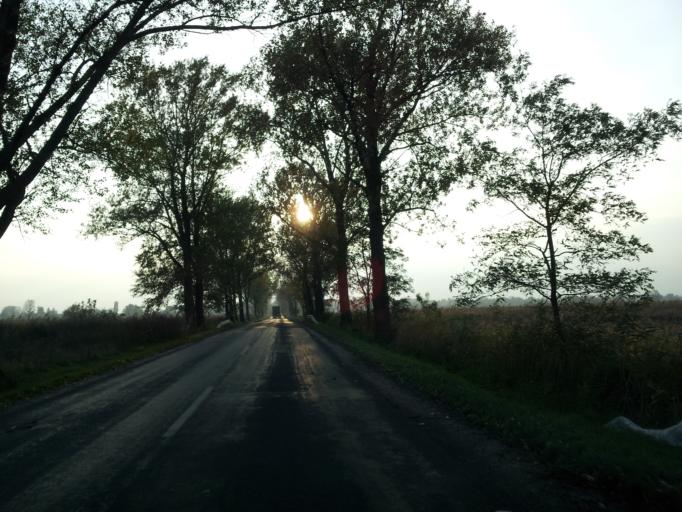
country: HU
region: Komarom-Esztergom
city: Kisber
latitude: 47.4802
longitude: 17.9693
